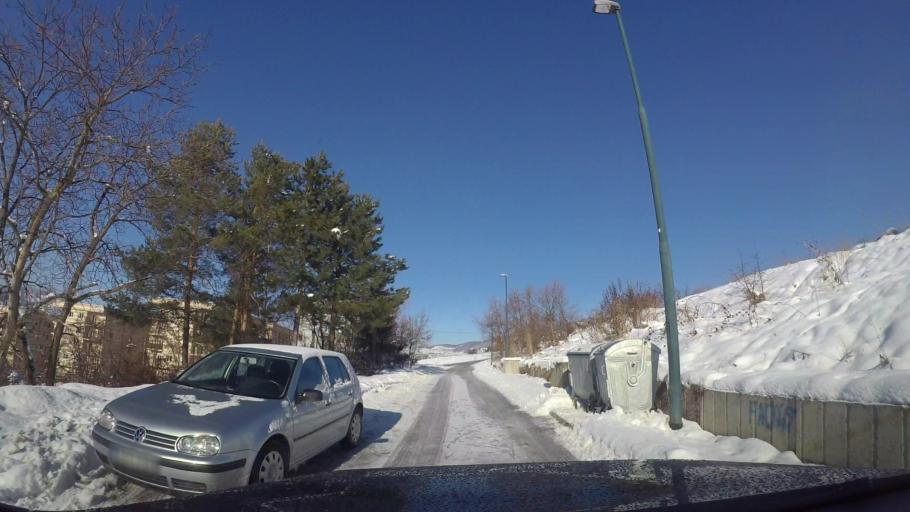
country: BA
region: Federation of Bosnia and Herzegovina
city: Kobilja Glava
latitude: 43.8810
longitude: 18.4101
